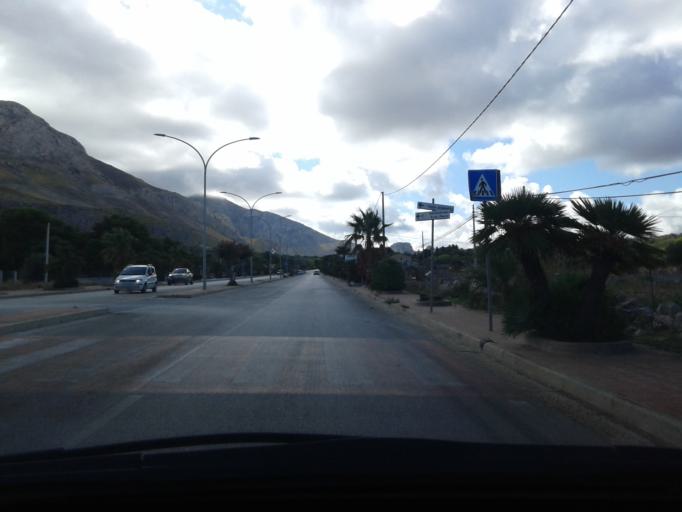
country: IT
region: Sicily
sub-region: Trapani
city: San Vito Lo Capo
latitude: 38.1634
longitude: 12.7361
